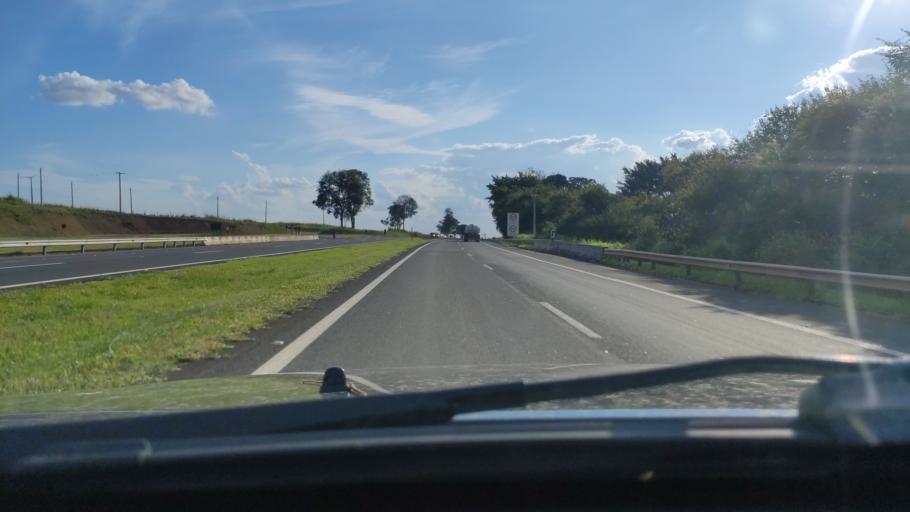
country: BR
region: Sao Paulo
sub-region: Itapira
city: Itapira
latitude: -22.4525
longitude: -46.8555
